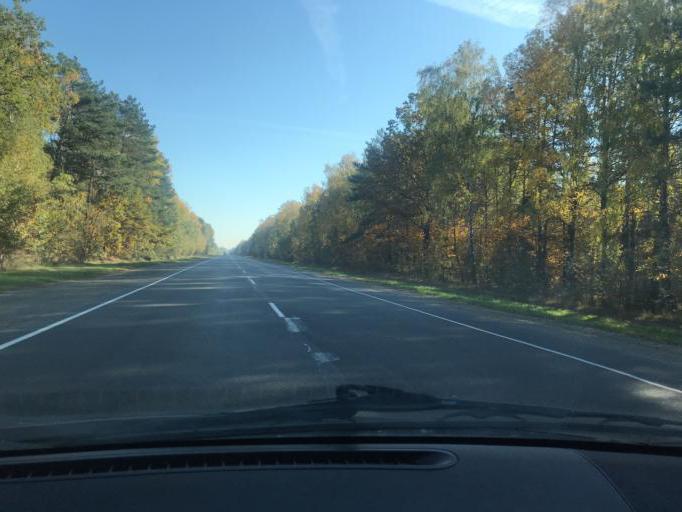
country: BY
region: Brest
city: Ivanava
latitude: 52.1544
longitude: 25.5948
